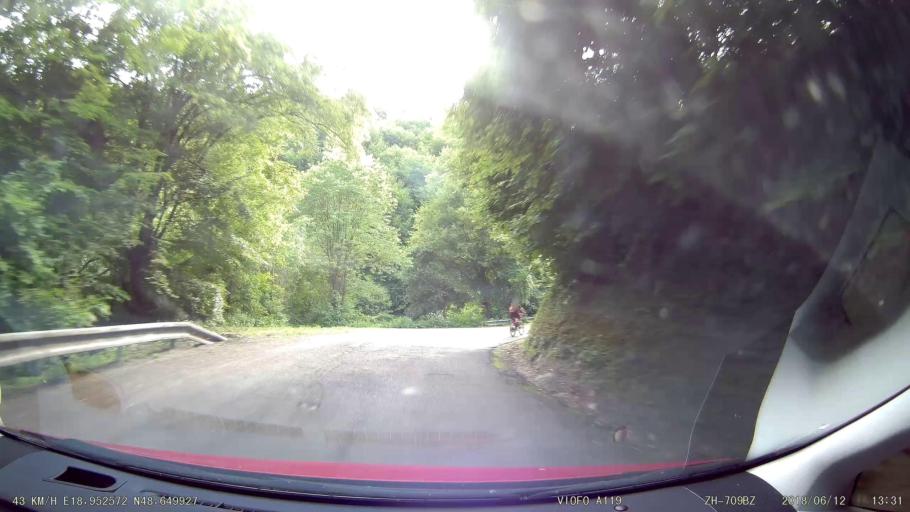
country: SK
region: Banskobystricky
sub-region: Okres Ziar nad Hronom
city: Kremnica
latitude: 48.6499
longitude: 18.9524
